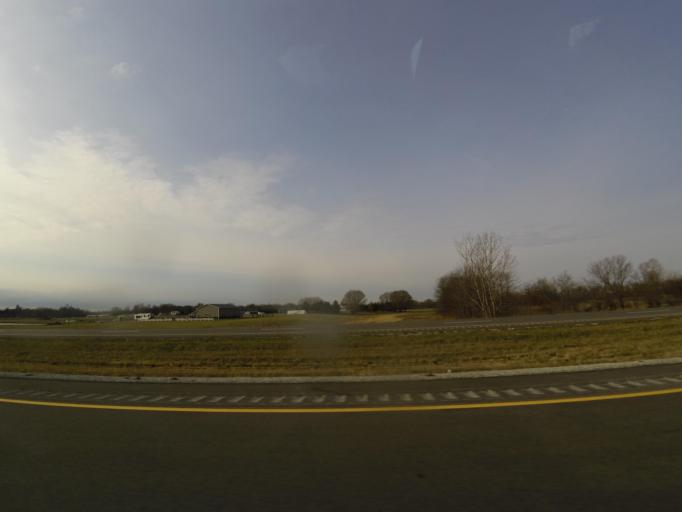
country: US
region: Illinois
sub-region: Shelby County
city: Moweaqua
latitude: 39.6425
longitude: -89.0105
